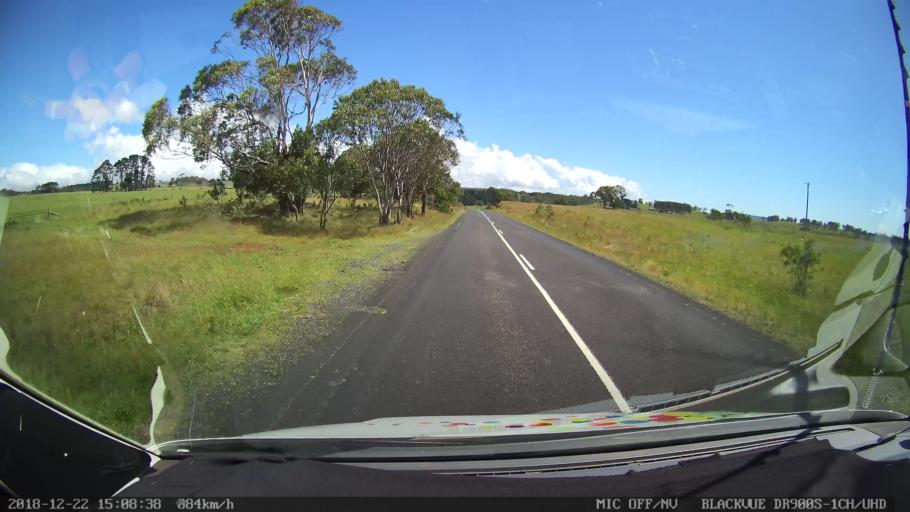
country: AU
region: New South Wales
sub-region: Bellingen
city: Dorrigo
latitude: -30.3148
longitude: 152.4131
